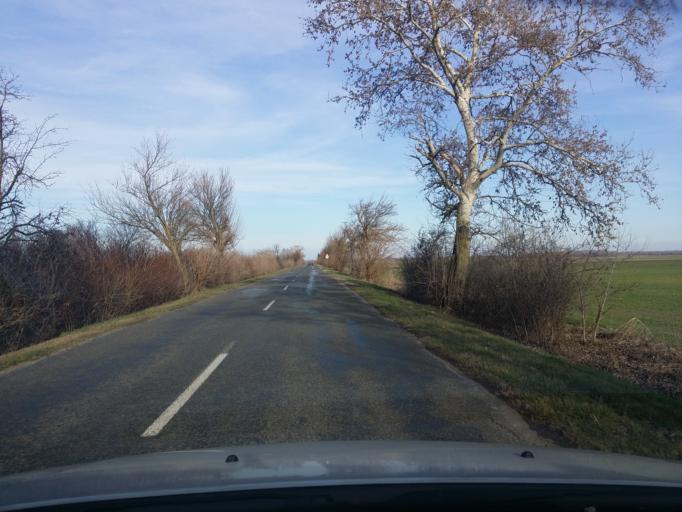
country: HU
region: Tolna
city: Madocsa
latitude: 46.6696
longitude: 18.9213
